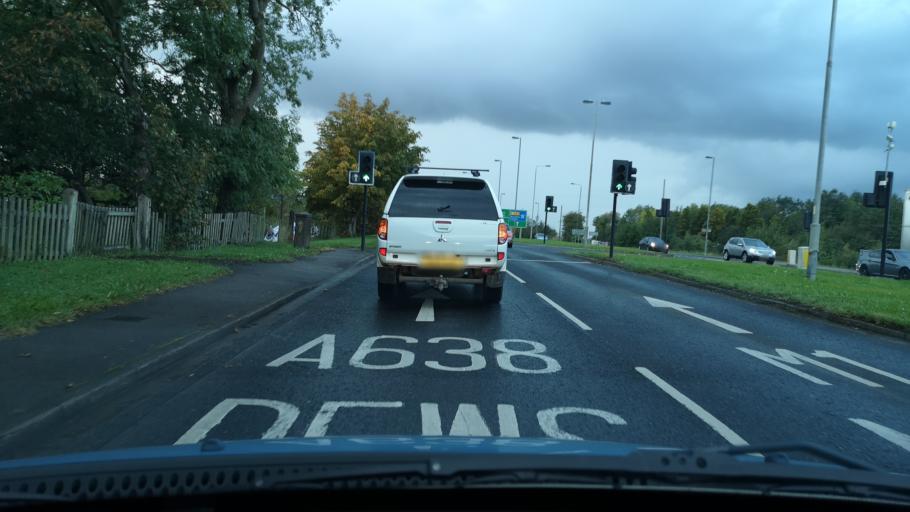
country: GB
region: England
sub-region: City and Borough of Wakefield
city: Horbury
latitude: 53.6827
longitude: -1.5513
